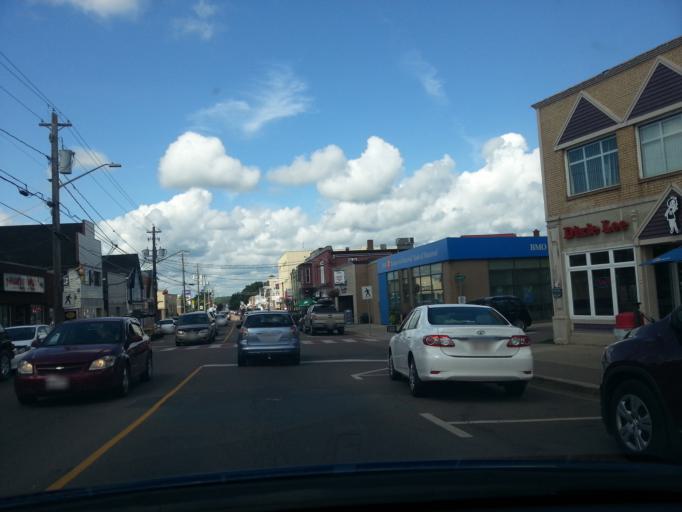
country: CA
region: New Brunswick
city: Shediac
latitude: 46.2195
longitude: -64.5420
